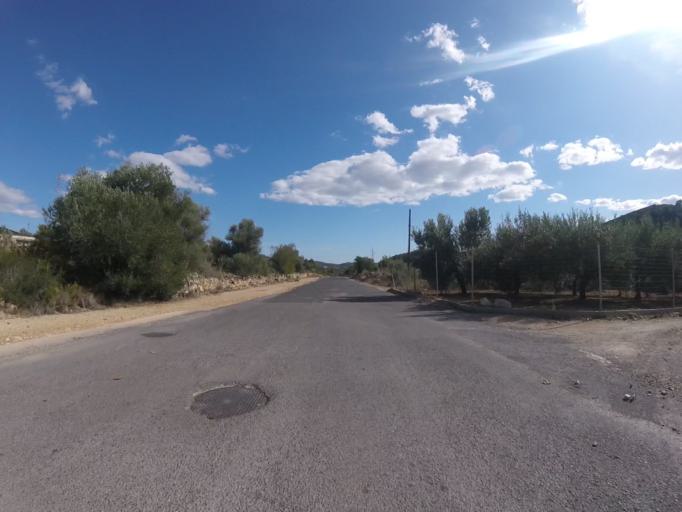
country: ES
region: Valencia
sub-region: Provincia de Castello
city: Alcala de Xivert
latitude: 40.2759
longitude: 0.2296
